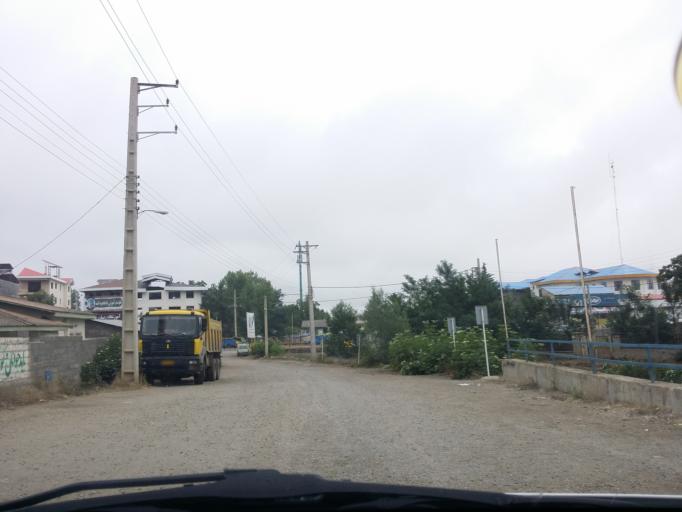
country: IR
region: Mazandaran
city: `Abbasabad
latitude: 36.5067
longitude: 51.1574
